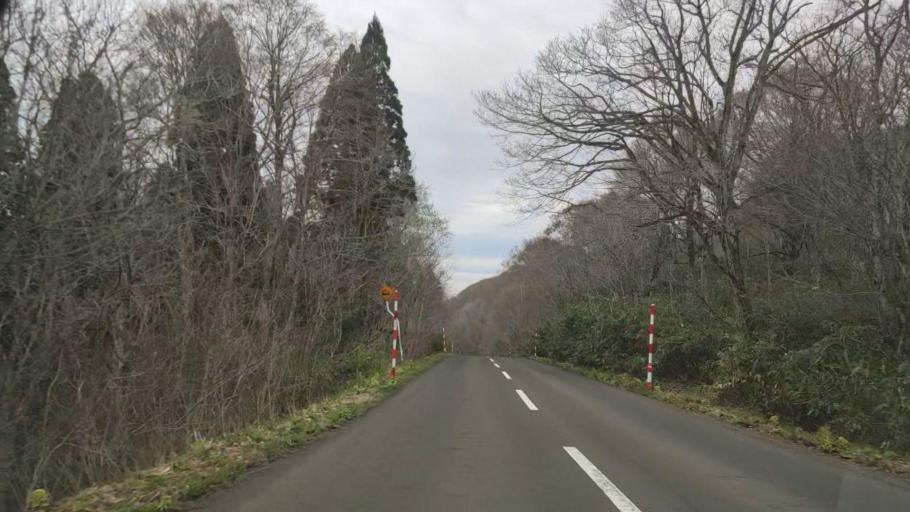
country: JP
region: Akita
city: Hanawa
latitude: 40.4148
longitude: 140.8194
